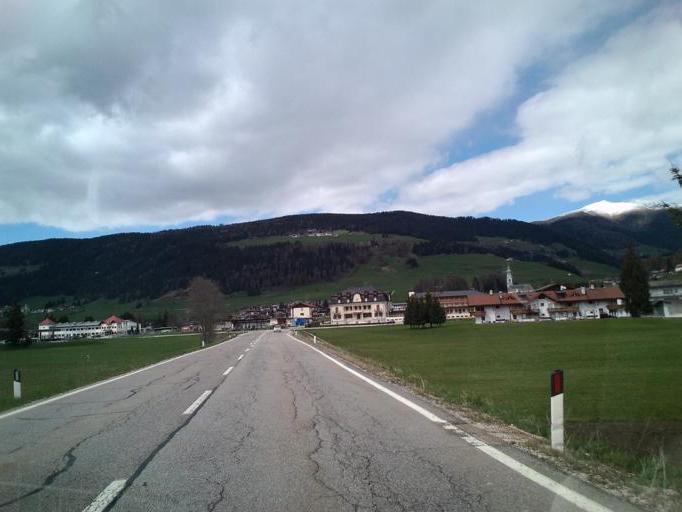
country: IT
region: Trentino-Alto Adige
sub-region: Bolzano
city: Dobbiaco
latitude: 46.7268
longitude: 12.2208
